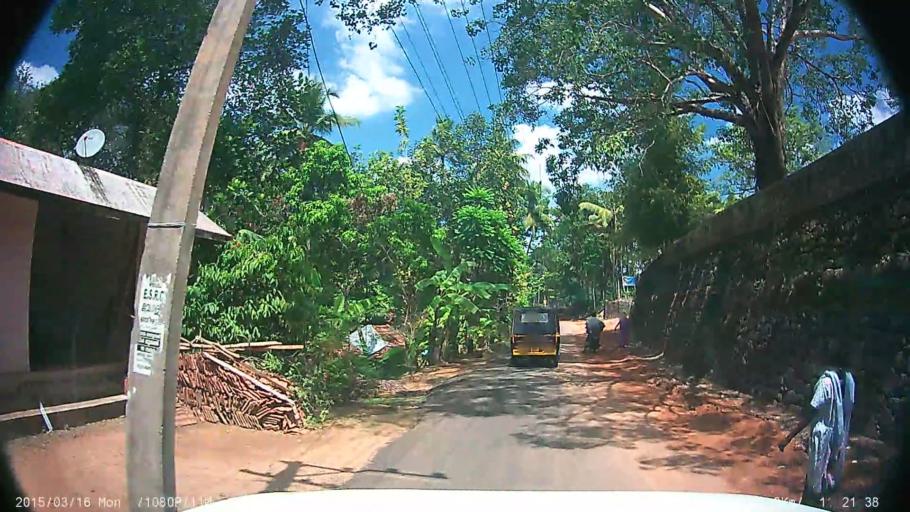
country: IN
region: Kerala
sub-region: Ernakulam
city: Piravam
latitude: 9.7921
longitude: 76.5476
